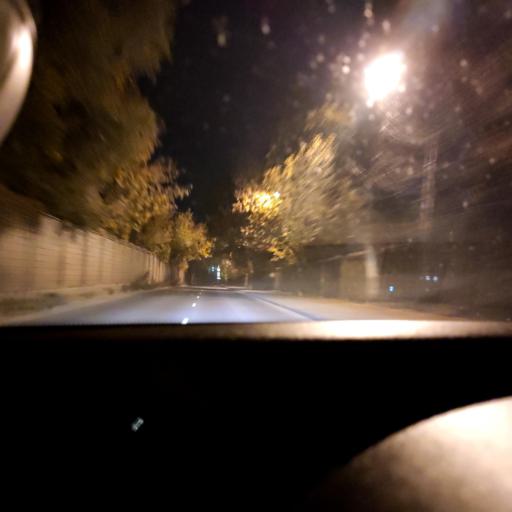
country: RU
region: Samara
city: Petra-Dubrava
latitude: 53.2397
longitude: 50.2715
